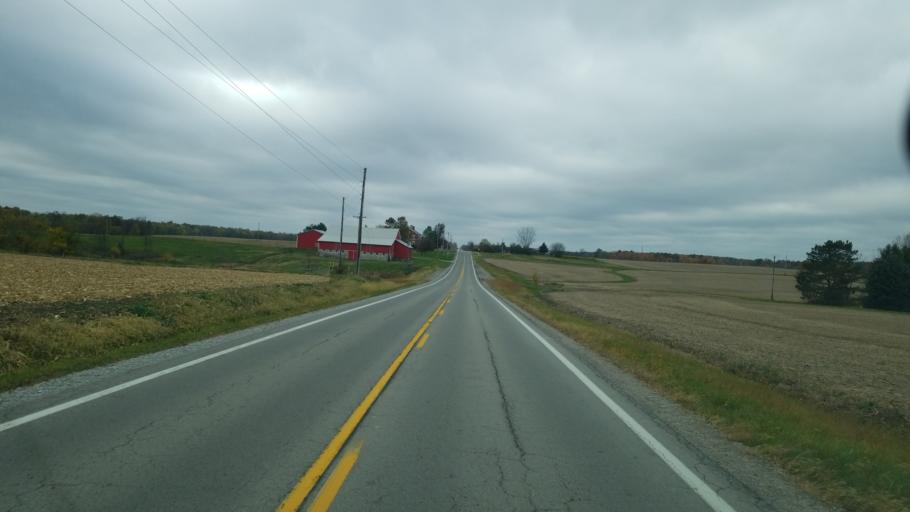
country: US
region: Ohio
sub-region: Sandusky County
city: Green Springs
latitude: 41.0812
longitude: -82.9720
